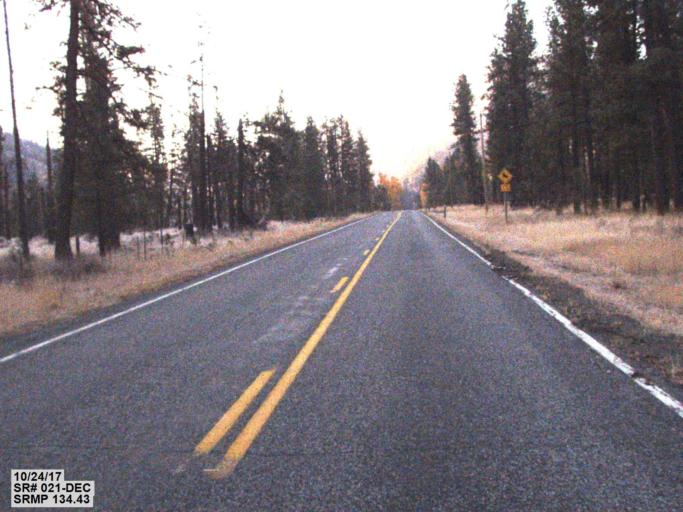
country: US
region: Washington
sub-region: Ferry County
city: Republic
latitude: 48.3126
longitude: -118.7391
